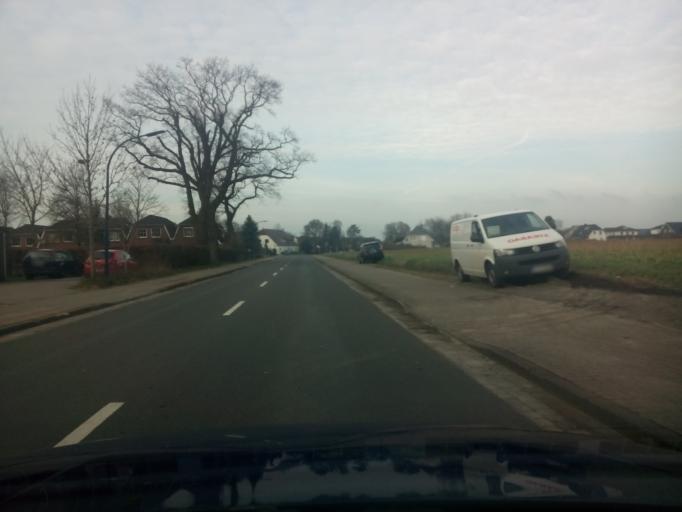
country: DE
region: Lower Saxony
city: Oyten
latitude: 53.0656
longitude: 9.0202
